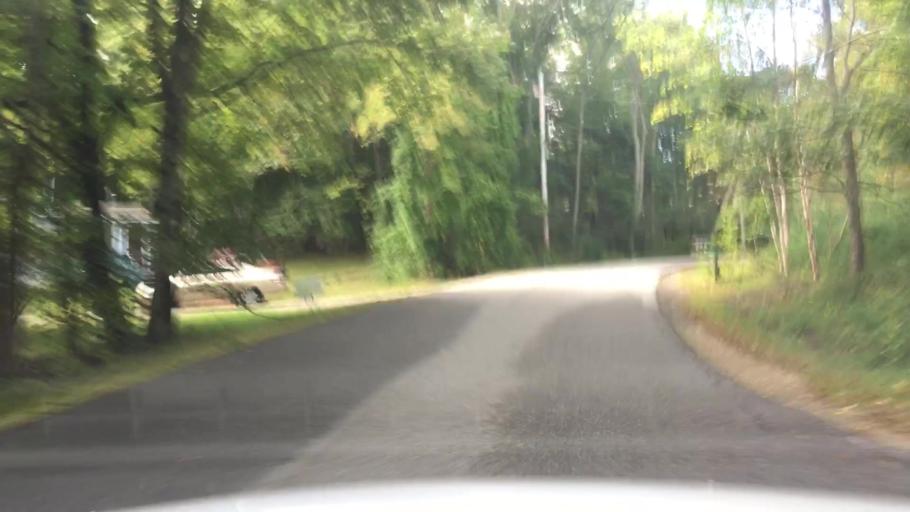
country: US
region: Maine
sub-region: York County
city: Kittery Point
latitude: 43.1113
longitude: -70.6862
